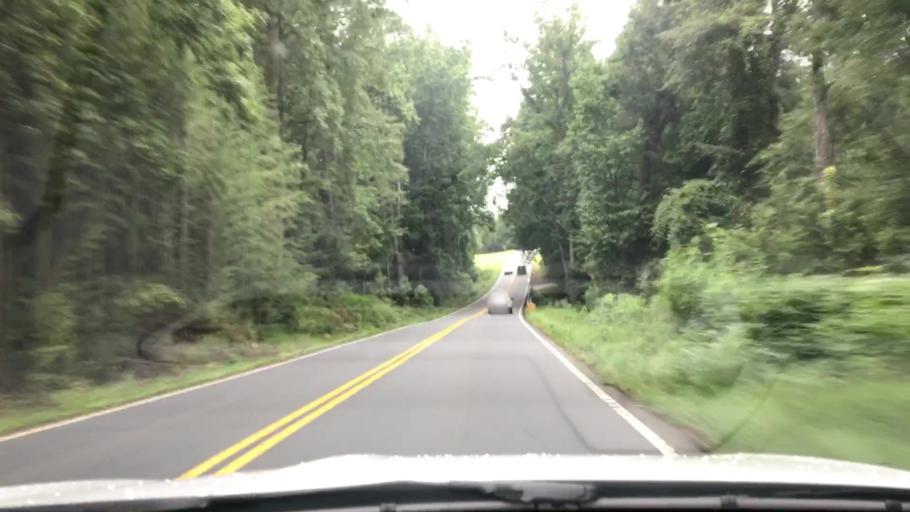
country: US
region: South Carolina
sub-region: Spartanburg County
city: Roebuck
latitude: 34.8345
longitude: -81.9651
